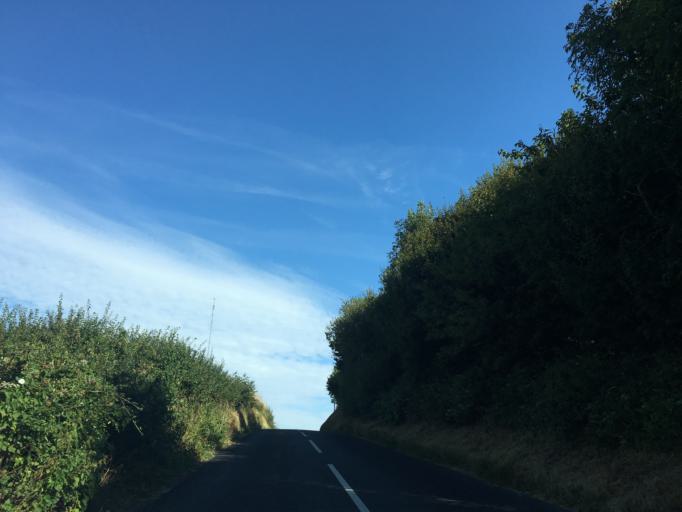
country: GB
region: England
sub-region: Isle of Wight
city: Chale
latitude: 50.6422
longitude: -1.3188
